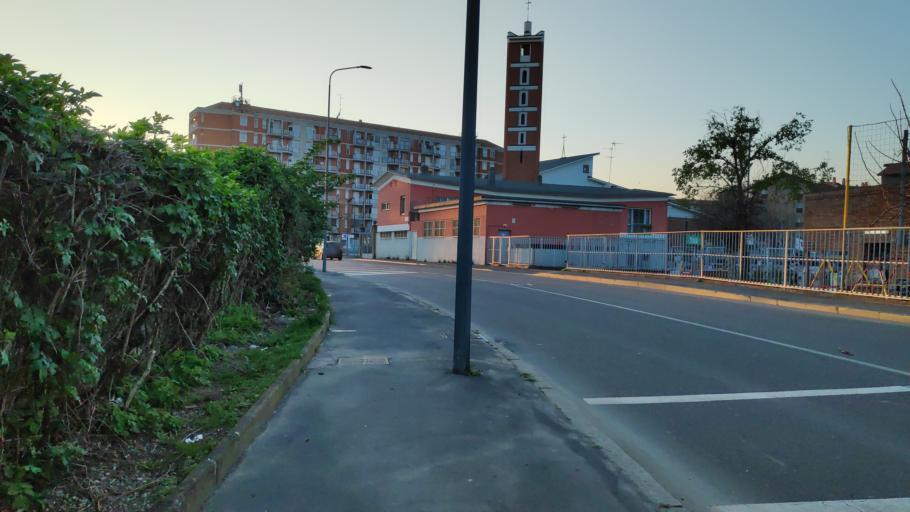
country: IT
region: Lombardy
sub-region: Citta metropolitana di Milano
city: Linate
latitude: 45.4450
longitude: 9.2502
